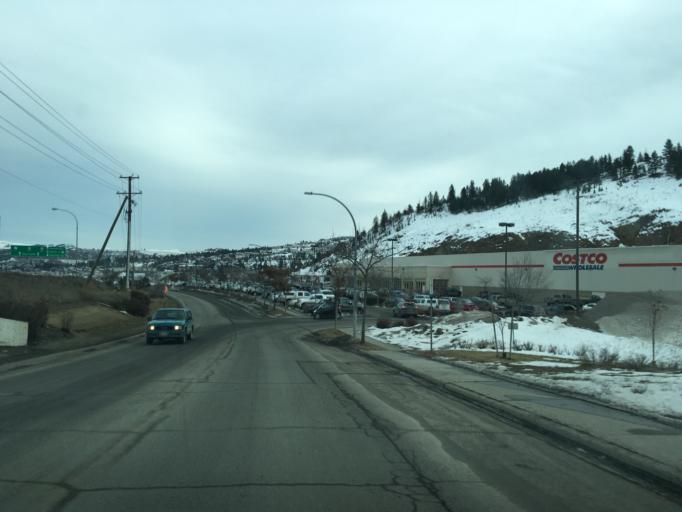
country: CA
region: British Columbia
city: Kamloops
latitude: 50.6561
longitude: -120.3902
